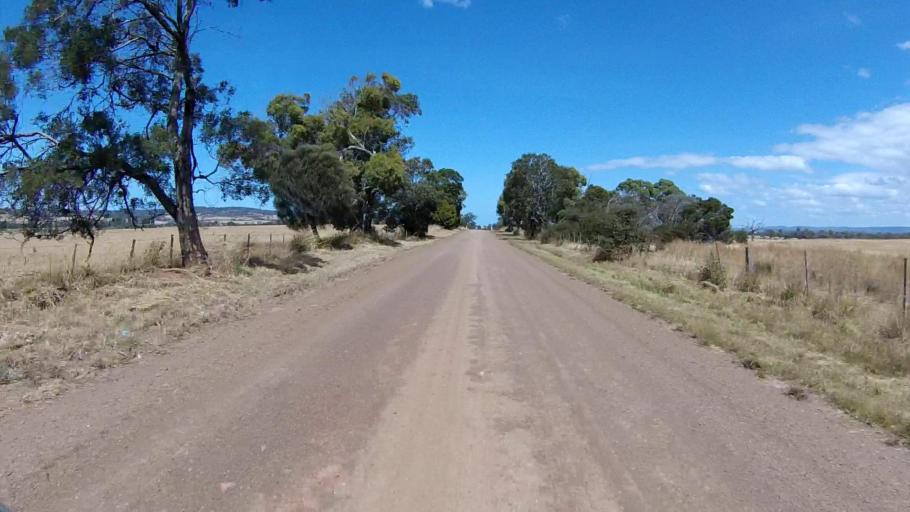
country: AU
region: Tasmania
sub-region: Break O'Day
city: St Helens
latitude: -41.9912
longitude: 148.0669
